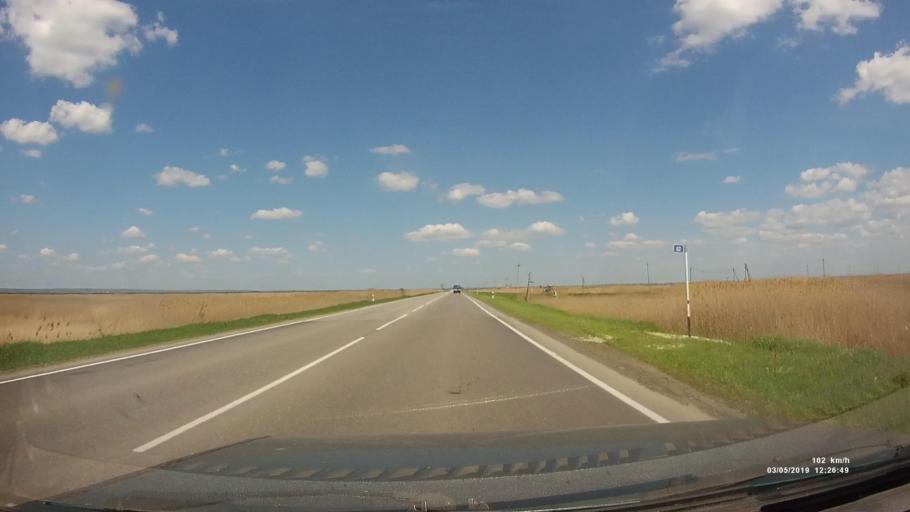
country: RU
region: Rostov
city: Semikarakorsk
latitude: 47.4506
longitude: 40.7166
